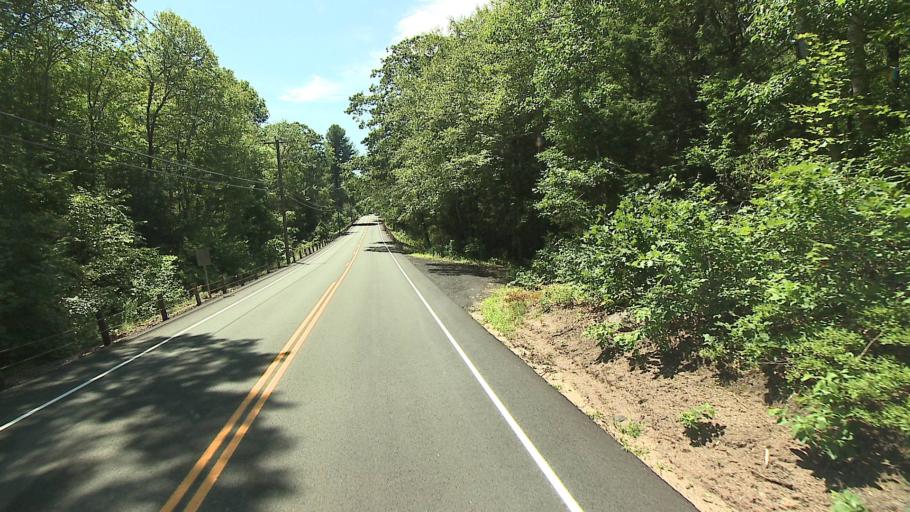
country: US
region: Connecticut
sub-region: Litchfield County
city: New Hartford Center
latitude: 41.9423
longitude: -72.9184
